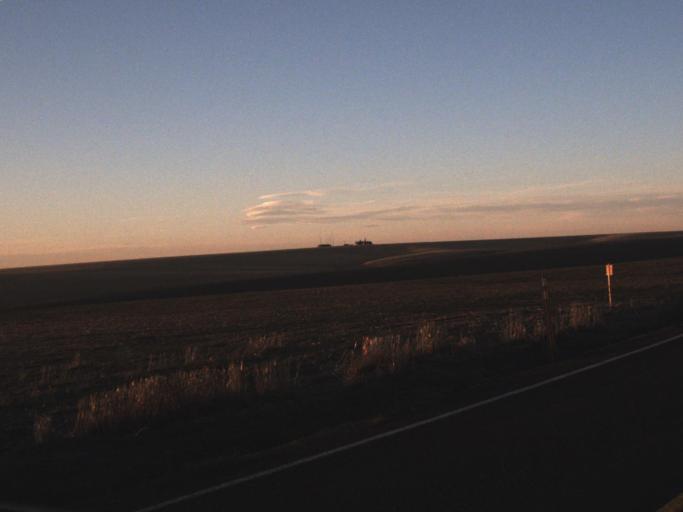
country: US
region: Washington
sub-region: Adams County
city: Ritzville
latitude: 46.9998
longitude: -118.6637
